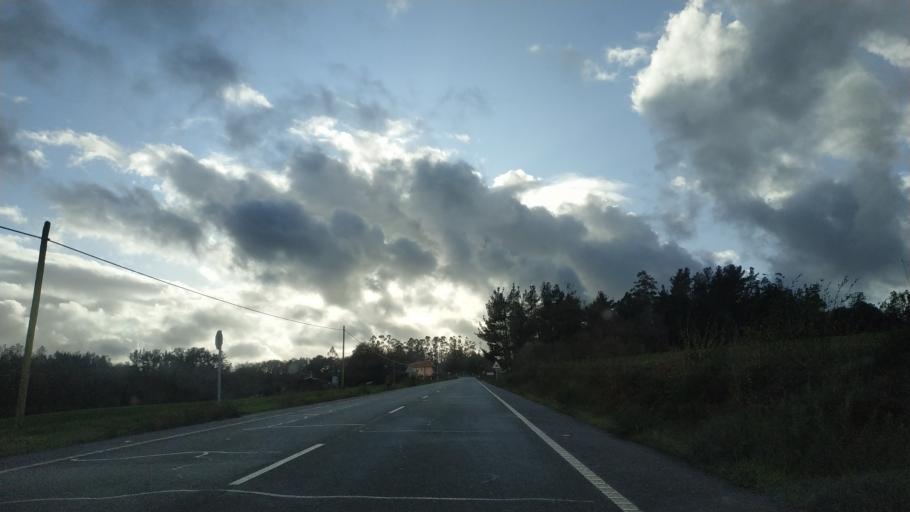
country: ES
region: Galicia
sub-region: Provincia da Coruna
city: Arzua
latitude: 42.8802
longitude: -8.2005
